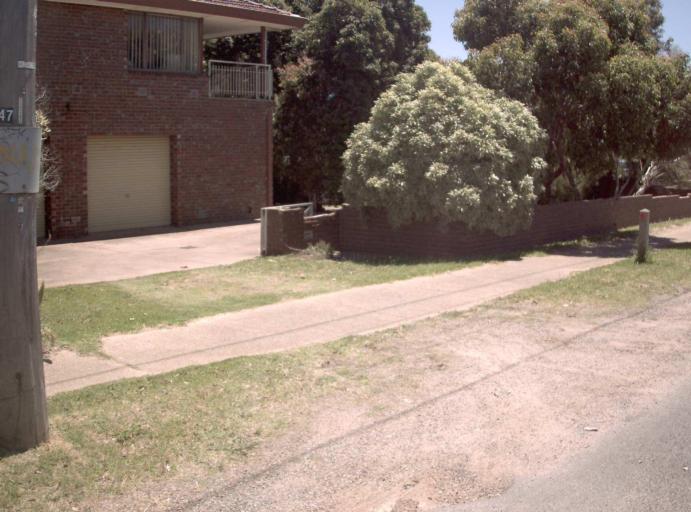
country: AU
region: Victoria
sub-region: Mornington Peninsula
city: Mornington
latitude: -38.2414
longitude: 145.0366
